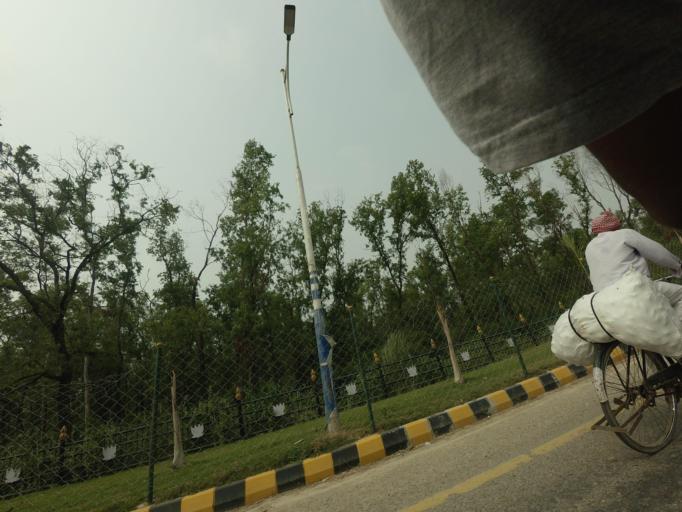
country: IN
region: Uttar Pradesh
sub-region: Maharajganj
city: Nautanwa
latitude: 27.4915
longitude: 83.2719
